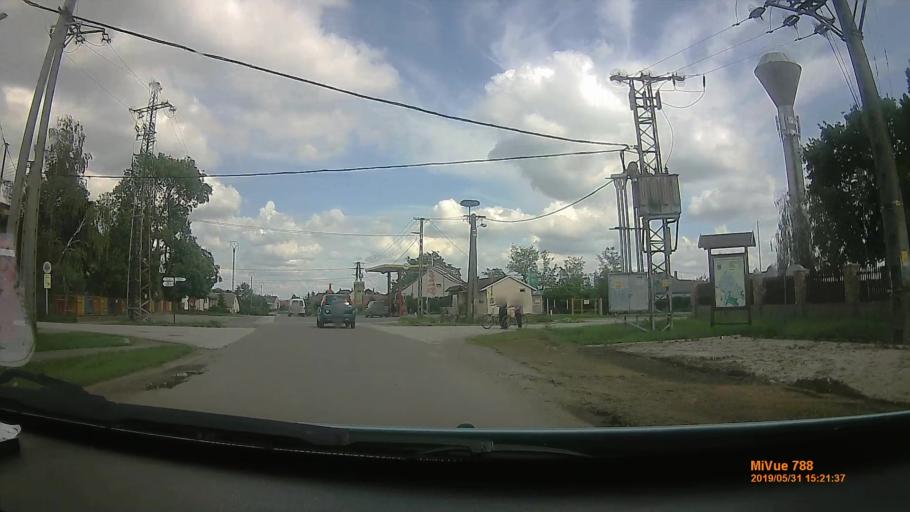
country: HU
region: Borsod-Abauj-Zemplen
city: Taktaharkany
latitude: 48.0840
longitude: 21.1295
